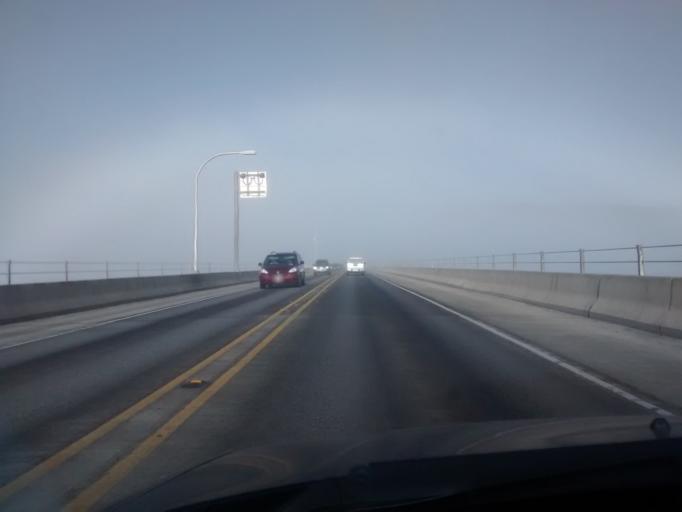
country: US
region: Washington
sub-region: Kitsap County
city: Lofall
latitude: 47.8625
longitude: -122.6292
